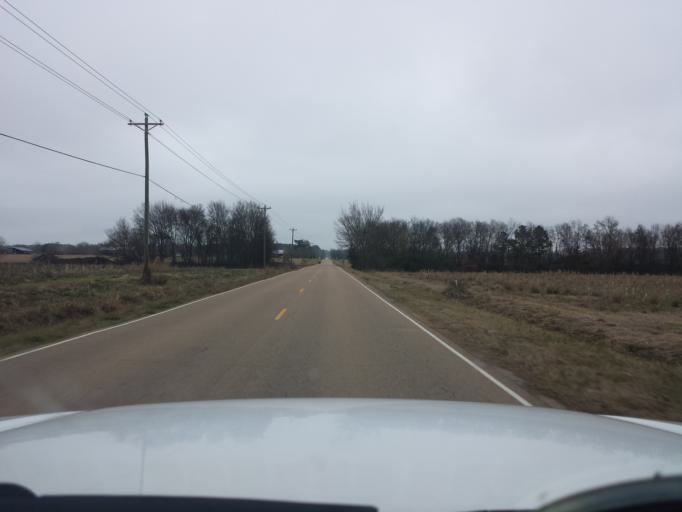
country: US
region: Mississippi
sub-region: Madison County
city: Madison
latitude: 32.4214
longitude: -89.9899
